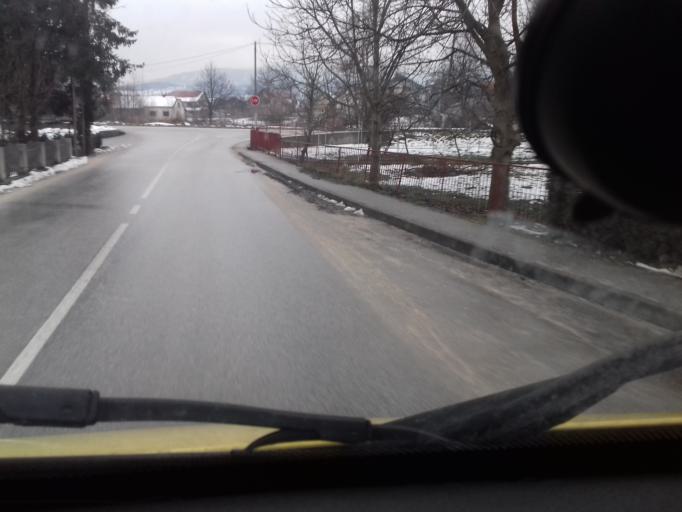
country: BA
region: Federation of Bosnia and Herzegovina
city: Vitez
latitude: 44.1685
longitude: 17.7679
